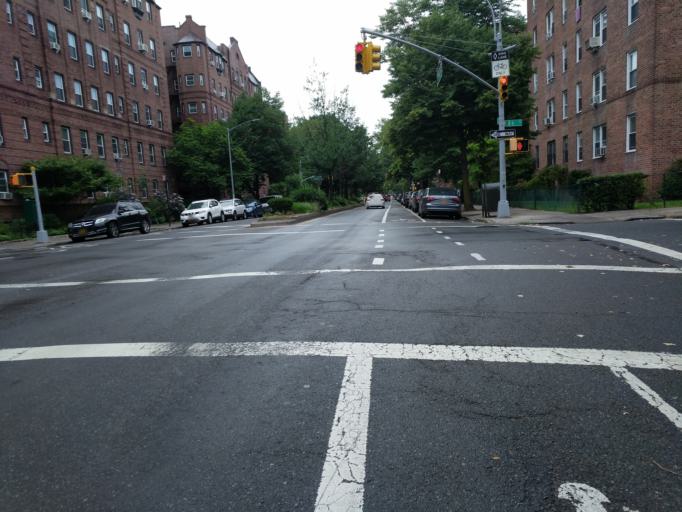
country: US
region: New York
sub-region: Queens County
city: Long Island City
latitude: 40.7542
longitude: -73.8809
